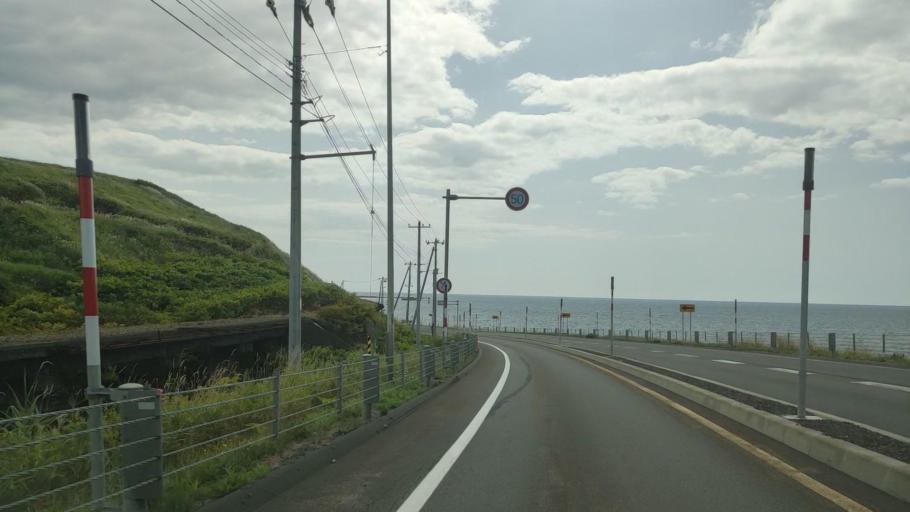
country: JP
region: Hokkaido
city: Rumoi
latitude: 44.5464
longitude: 141.7671
